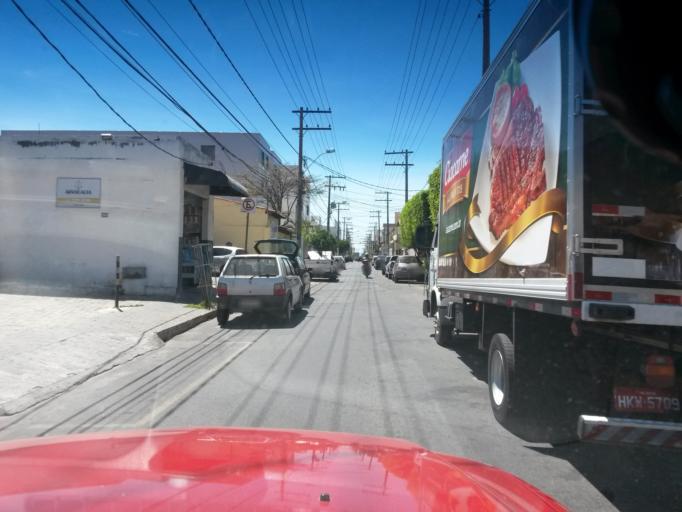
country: BR
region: Minas Gerais
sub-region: Belo Horizonte
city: Belo Horizonte
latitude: -19.9052
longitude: -43.9774
